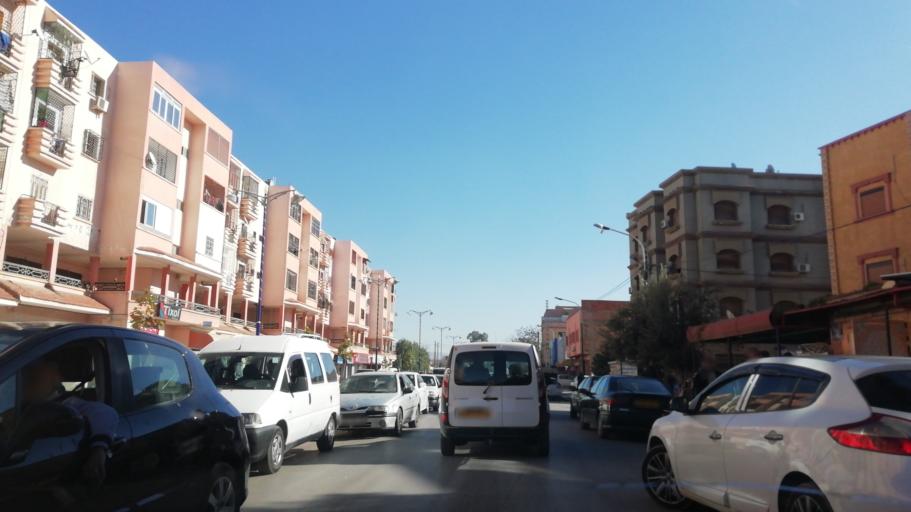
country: DZ
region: Tlemcen
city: Nedroma
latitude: 34.8448
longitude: -1.7219
